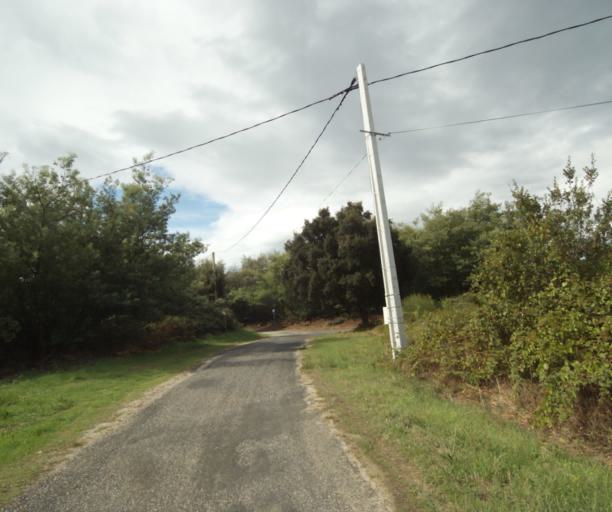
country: FR
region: Languedoc-Roussillon
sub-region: Departement des Pyrenees-Orientales
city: Argelers
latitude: 42.5354
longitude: 3.0426
